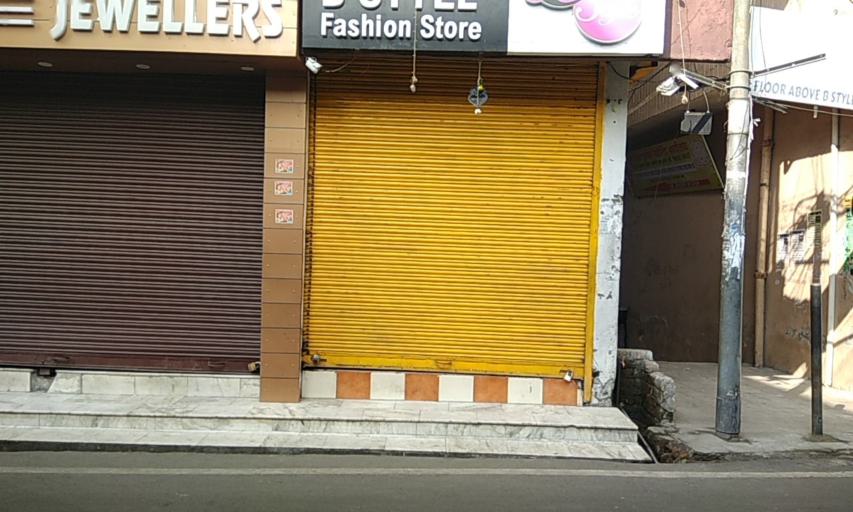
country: IN
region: Himachal Pradesh
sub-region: Kangra
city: Palampur
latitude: 32.1081
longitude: 76.5354
